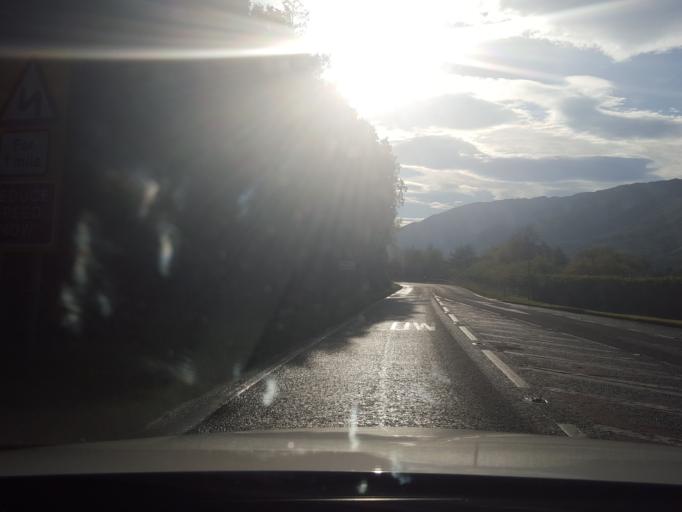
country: GB
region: Scotland
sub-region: Highland
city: Fort William
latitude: 57.2736
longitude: -5.5125
